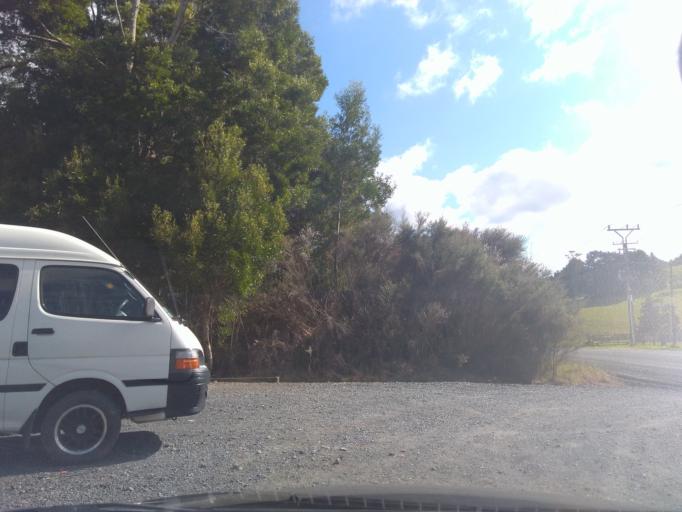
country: NZ
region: Northland
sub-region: Whangarei
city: Whangarei
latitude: -35.7046
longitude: 174.3537
